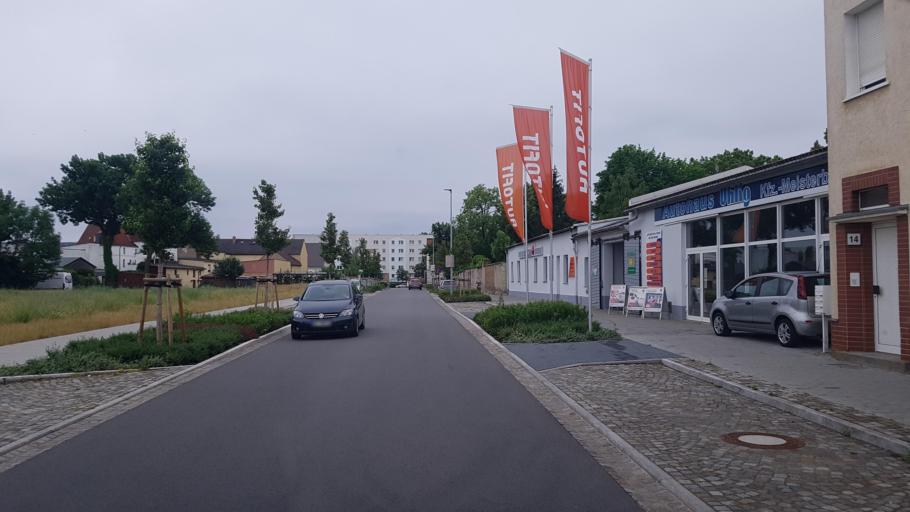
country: DE
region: Brandenburg
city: Senftenberg
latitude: 51.5211
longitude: 13.9982
